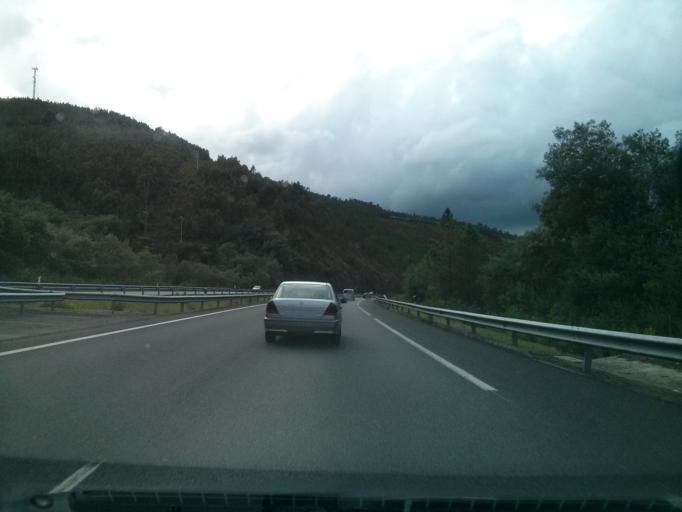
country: ES
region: Galicia
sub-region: Provincia de Ourense
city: Toen
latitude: 42.3343
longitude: -7.9789
